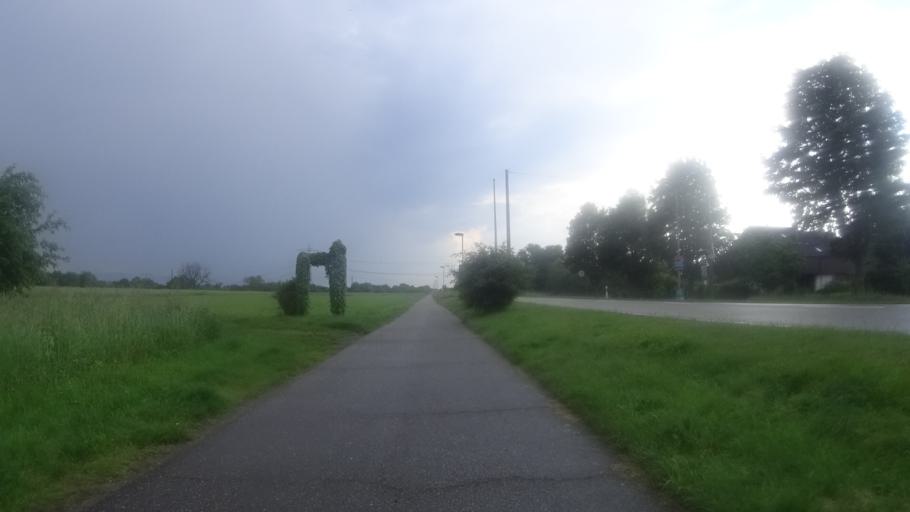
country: DE
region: Baden-Wuerttemberg
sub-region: Karlsruhe Region
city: Durmersheim
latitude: 48.9231
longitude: 8.2627
